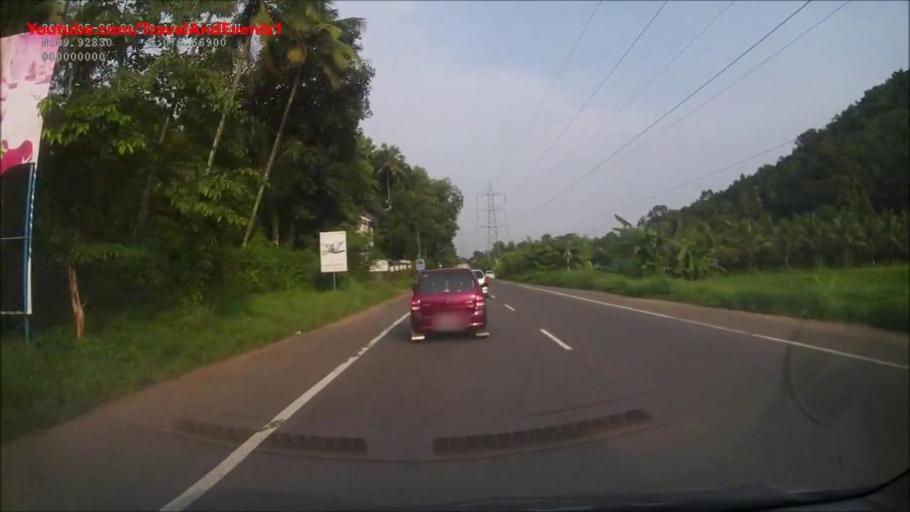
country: IN
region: Kerala
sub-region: Ernakulam
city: Muvattupula
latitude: 9.9268
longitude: 76.6707
